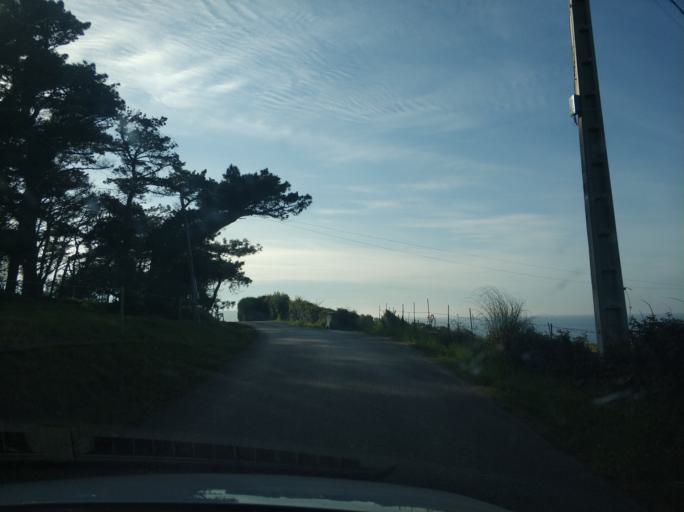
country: ES
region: Cantabria
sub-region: Provincia de Cantabria
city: Comillas
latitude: 43.3893
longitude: -4.3018
